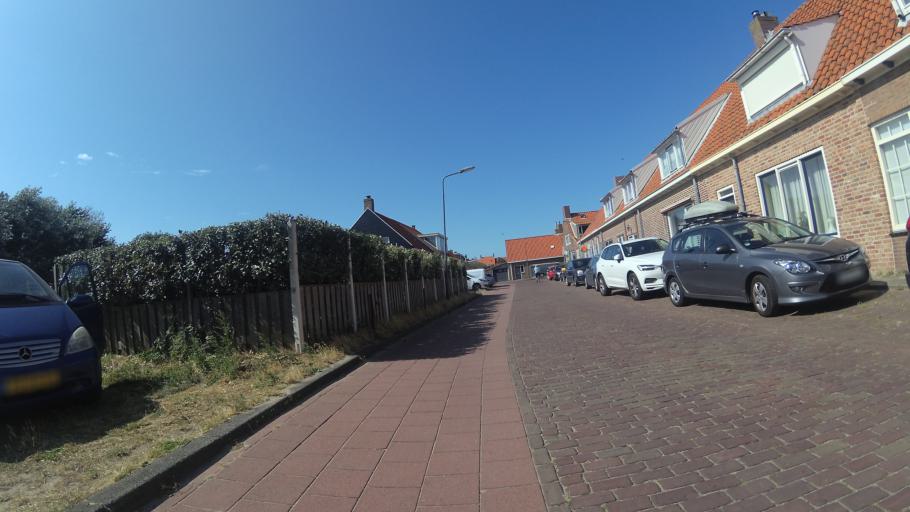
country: NL
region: Zeeland
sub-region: Gemeente Vlissingen
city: Vlissingen
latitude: 51.5259
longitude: 3.4410
